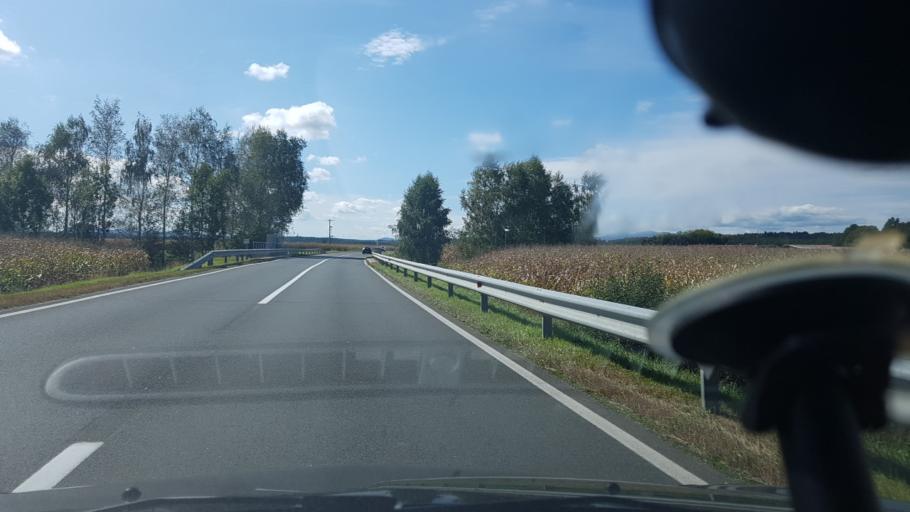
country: SI
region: Slovenska Bistrica
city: Pragersko
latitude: 46.4024
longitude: 15.6533
